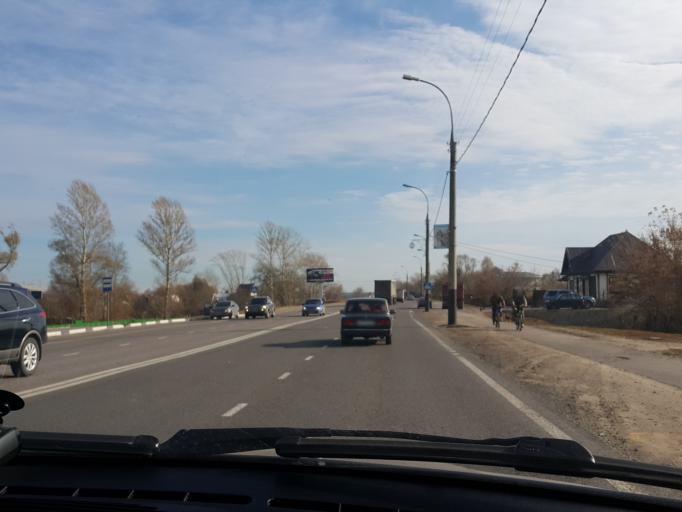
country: RU
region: Tambov
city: Tambov
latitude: 52.7233
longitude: 41.4756
